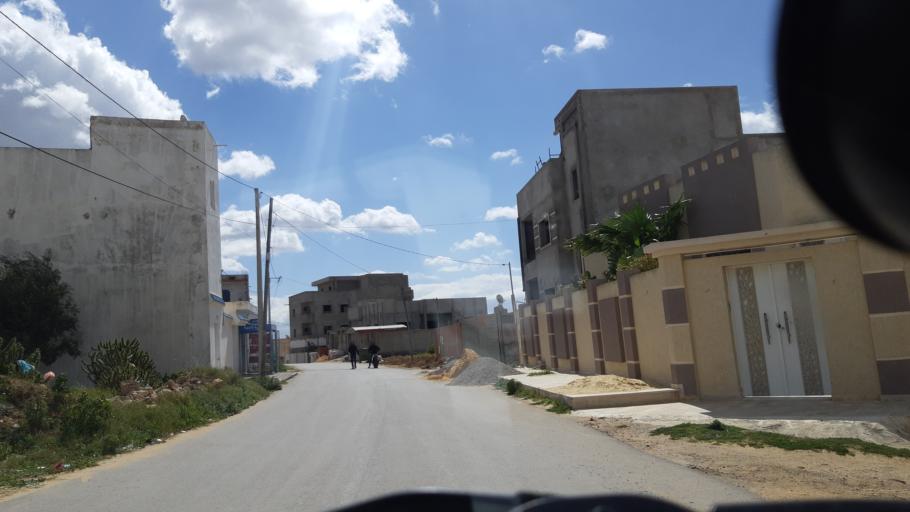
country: TN
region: Susah
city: Akouda
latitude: 35.8800
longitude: 10.5407
